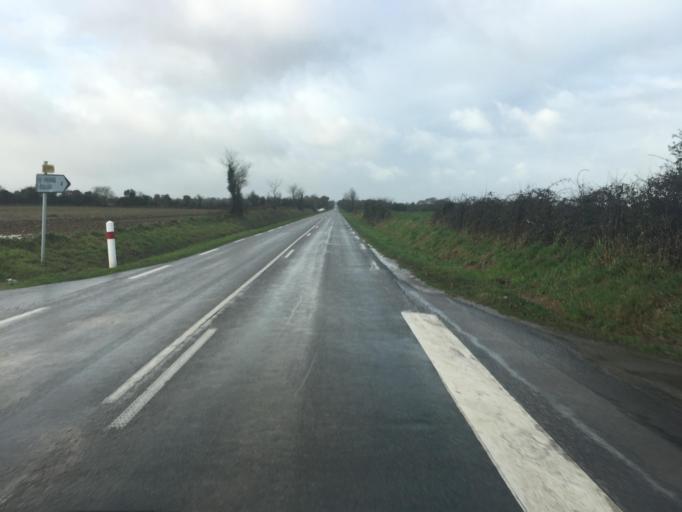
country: FR
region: Lower Normandy
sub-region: Departement de la Manche
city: Saint-Pierre-Eglise
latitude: 49.6700
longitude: -1.3527
